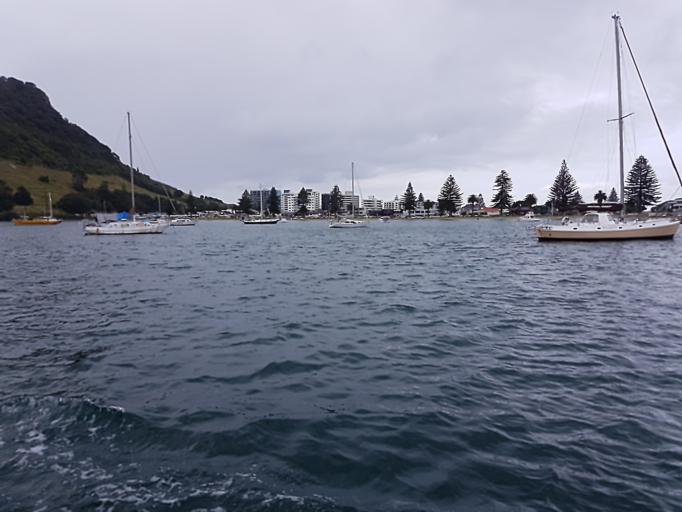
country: NZ
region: Bay of Plenty
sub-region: Tauranga City
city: Tauranga
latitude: -37.6390
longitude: 176.1779
